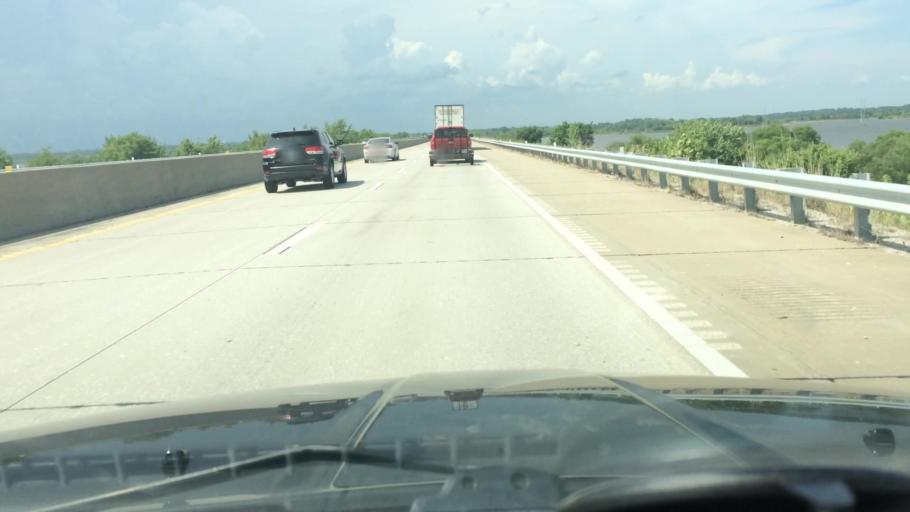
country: US
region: Missouri
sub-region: Henry County
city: Clinton
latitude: 38.3143
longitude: -93.7582
